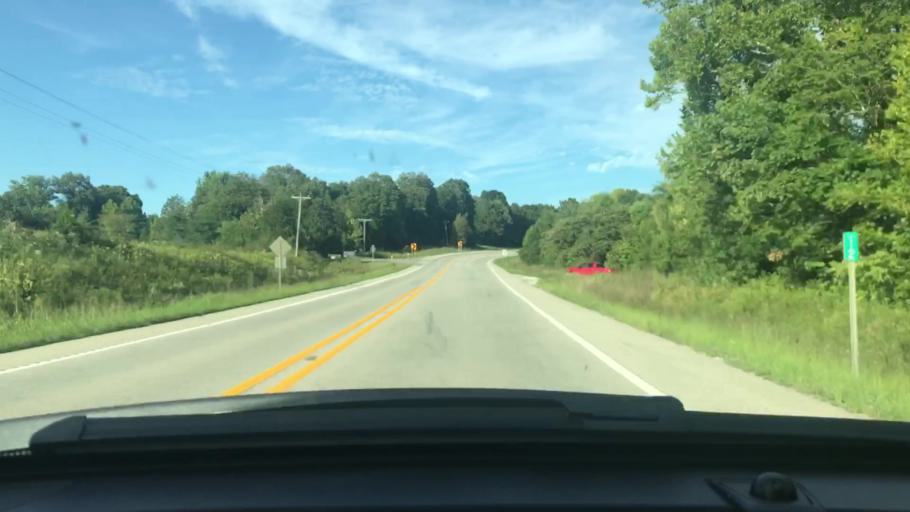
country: US
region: Arkansas
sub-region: Sharp County
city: Cherokee Village
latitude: 36.2752
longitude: -91.3297
